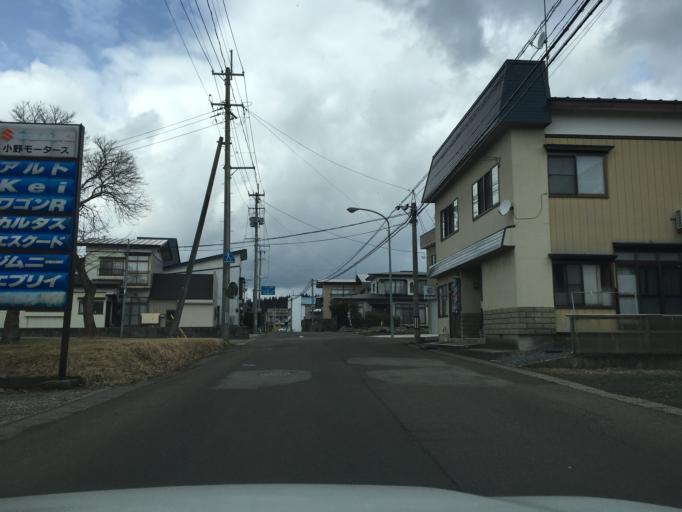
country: JP
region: Akita
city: Takanosu
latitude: 40.1597
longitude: 140.3316
